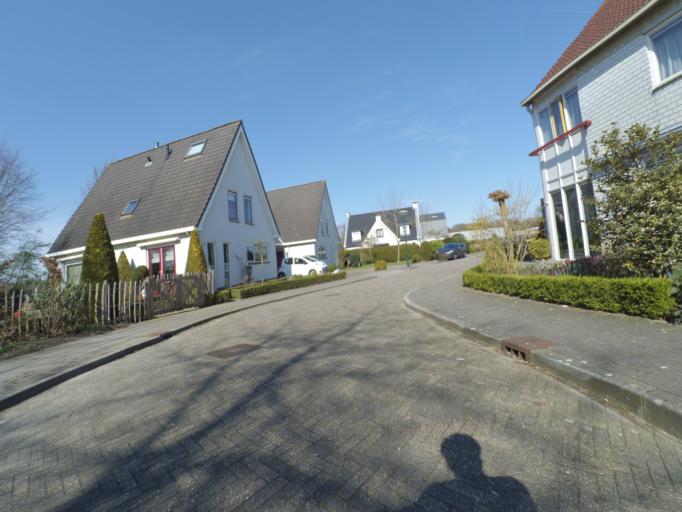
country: NL
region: Utrecht
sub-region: Gemeente Woudenberg
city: Woudenberg
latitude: 52.0857
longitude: 5.4086
